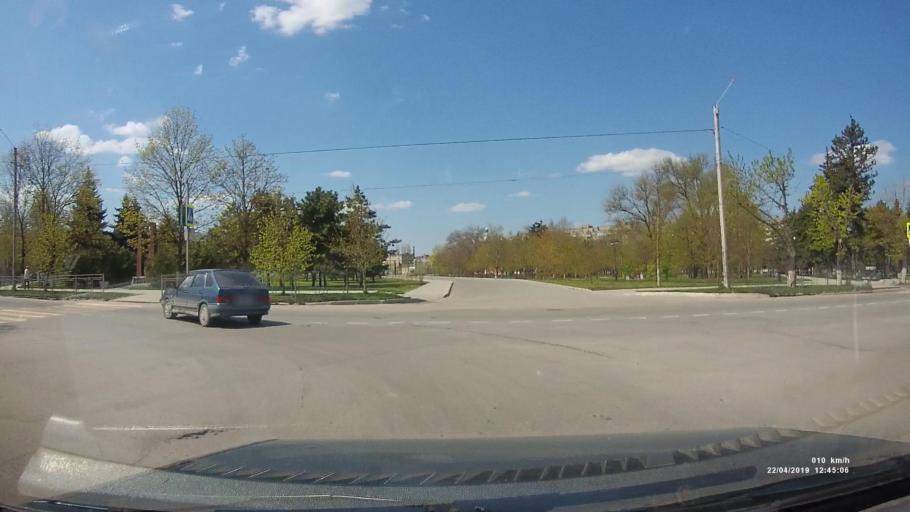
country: RU
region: Rostov
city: Azov
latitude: 47.1053
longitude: 39.4158
